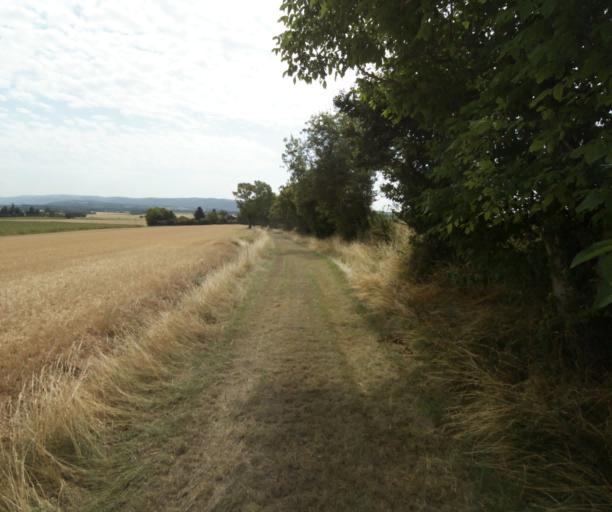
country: FR
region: Midi-Pyrenees
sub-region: Departement de la Haute-Garonne
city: Saint-Felix-Lauragais
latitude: 43.4398
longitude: 1.9021
